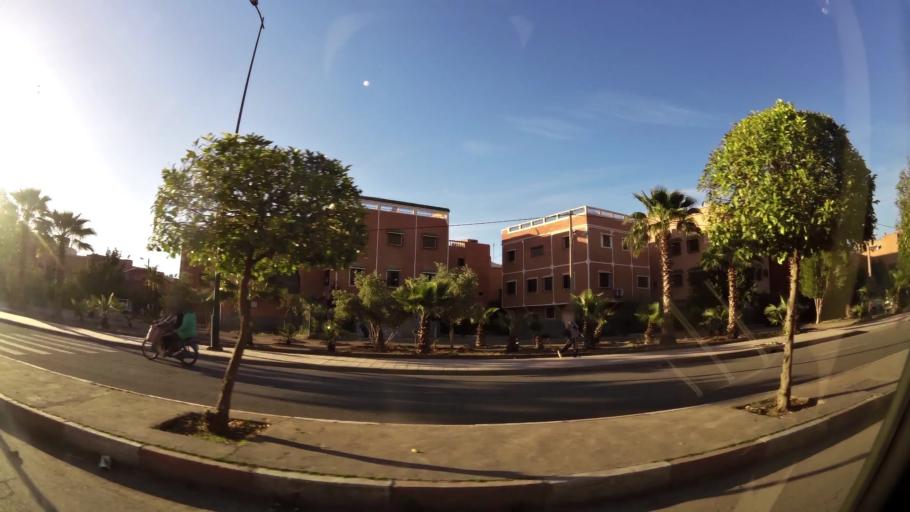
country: MA
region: Marrakech-Tensift-Al Haouz
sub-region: Marrakech
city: Marrakesh
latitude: 31.6219
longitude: -8.0559
